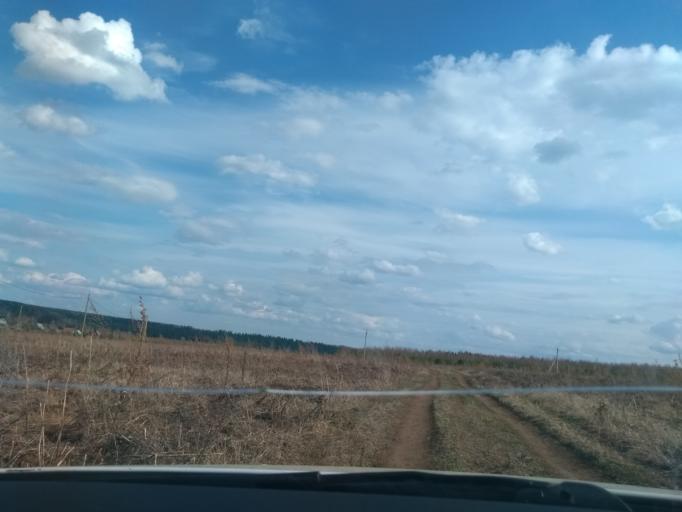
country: RU
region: Perm
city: Sylva
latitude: 57.8427
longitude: 56.7908
